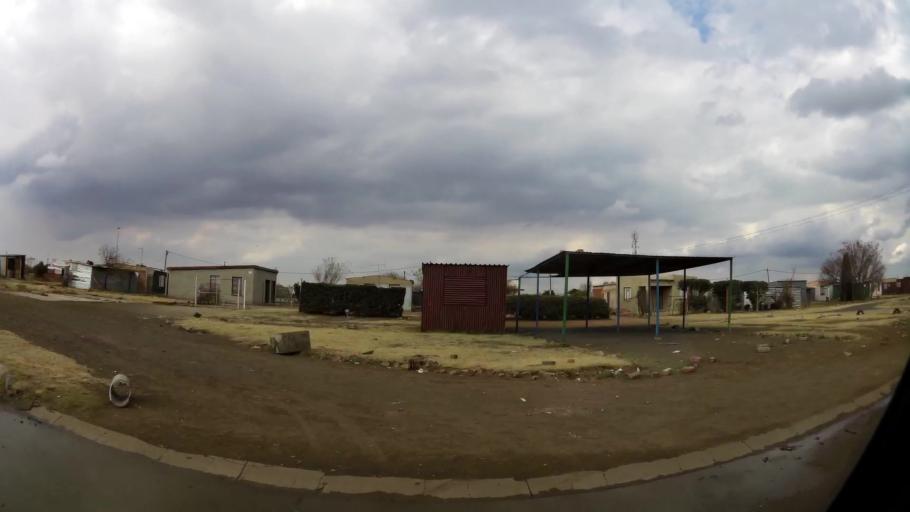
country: ZA
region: Gauteng
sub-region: Sedibeng District Municipality
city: Vanderbijlpark
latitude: -26.6941
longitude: 27.7839
